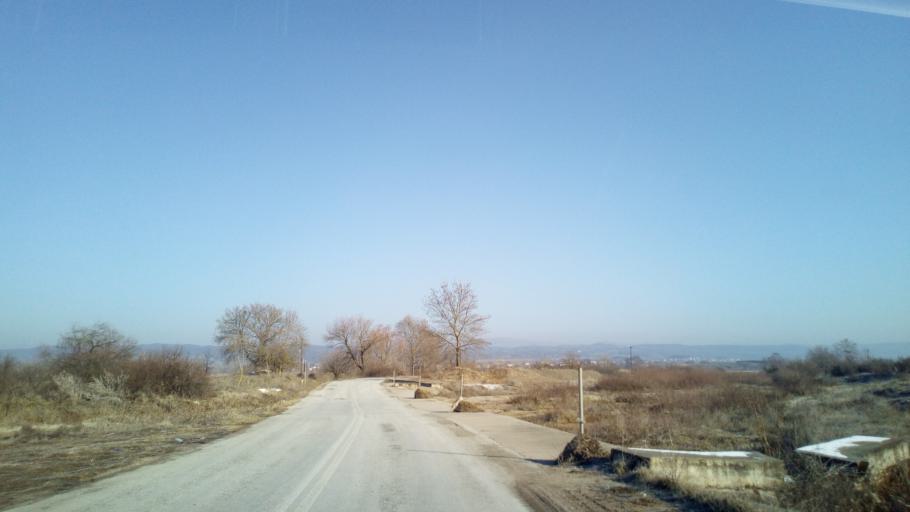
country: GR
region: Central Macedonia
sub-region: Nomos Thessalonikis
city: Gerakarou
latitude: 40.6579
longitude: 23.2510
